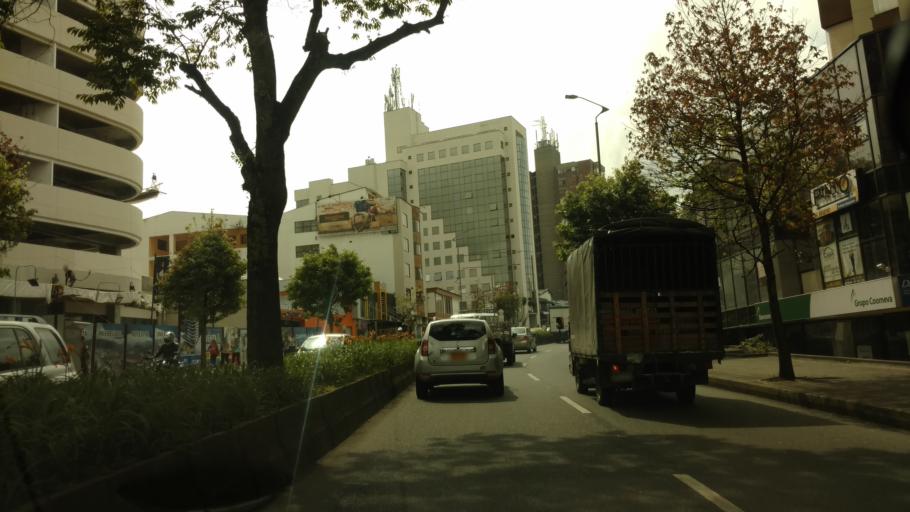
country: CO
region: Caldas
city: Villamaria
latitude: 5.0590
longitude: -75.4872
